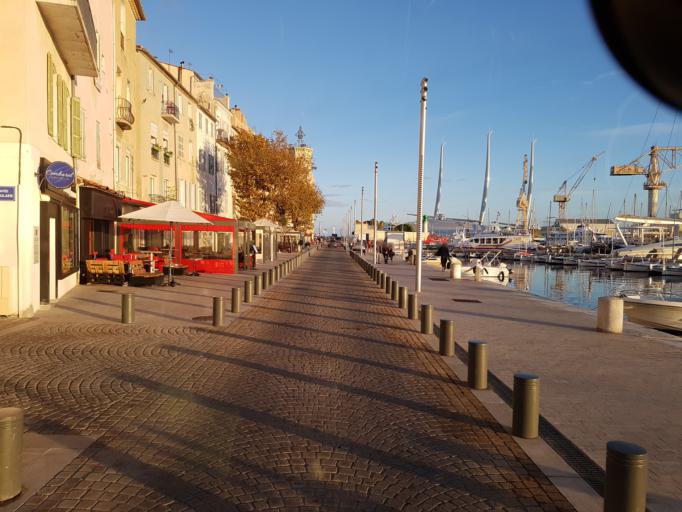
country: FR
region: Provence-Alpes-Cote d'Azur
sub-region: Departement des Bouches-du-Rhone
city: La Ciotat
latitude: 43.1744
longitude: 5.6082
